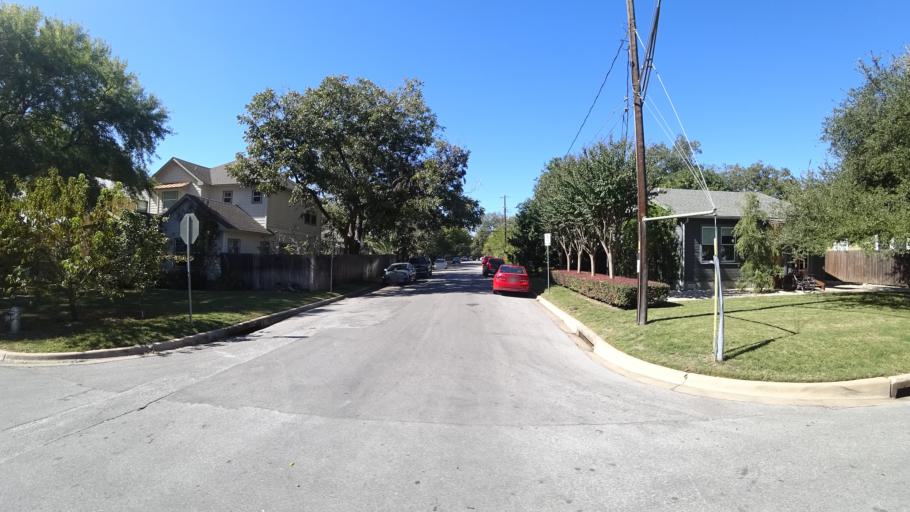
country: US
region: Texas
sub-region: Travis County
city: Austin
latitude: 30.3115
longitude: -97.7404
